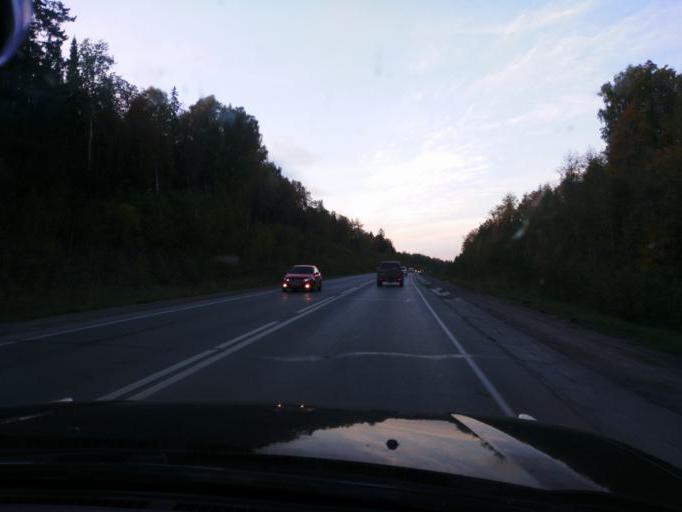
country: RU
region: Perm
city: Novyye Lyady
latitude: 58.0940
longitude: 56.4267
